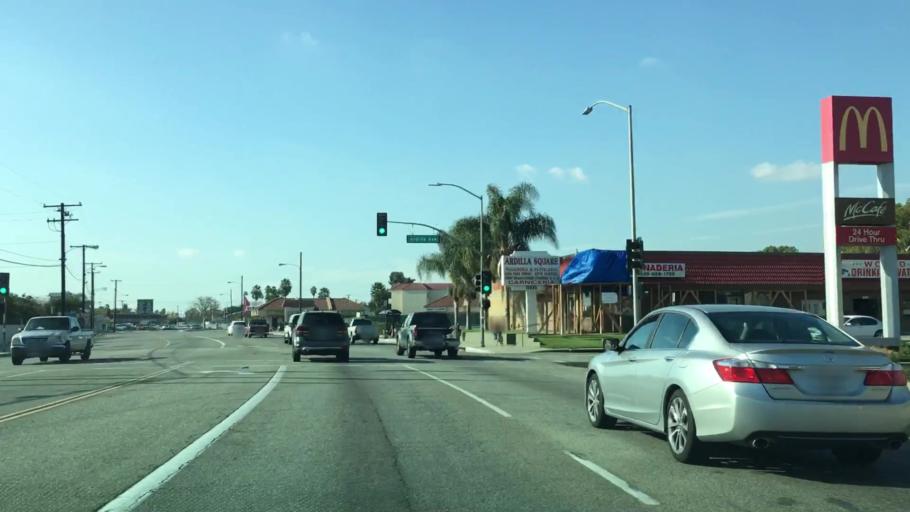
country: US
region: California
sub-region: Los Angeles County
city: West Puente Valley
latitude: 34.0535
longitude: -117.9744
